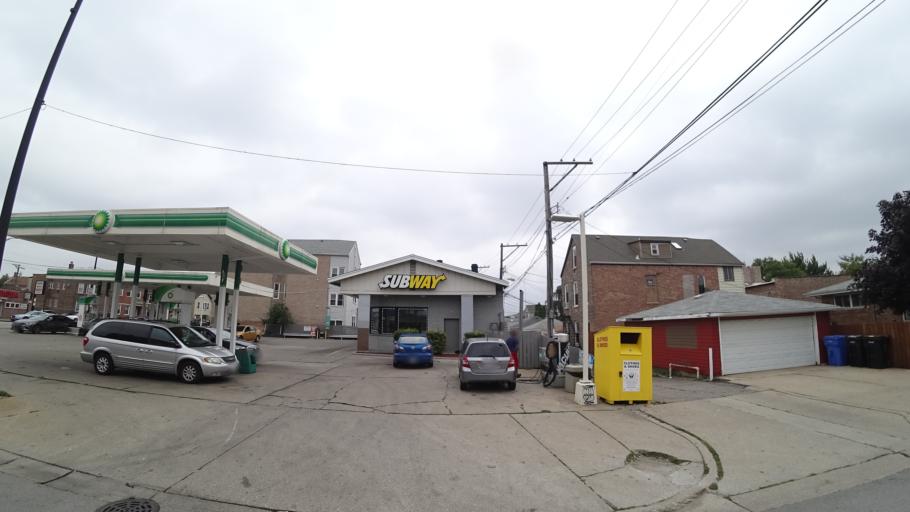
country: US
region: Illinois
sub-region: Cook County
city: Chicago
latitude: 41.8518
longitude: -87.6758
